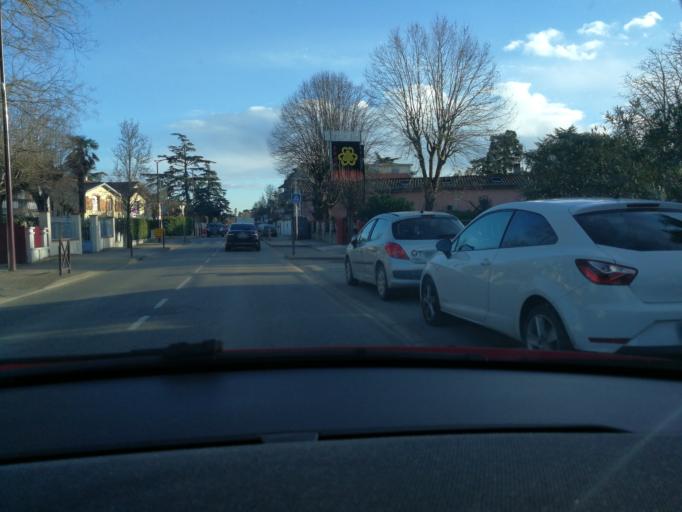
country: FR
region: Midi-Pyrenees
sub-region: Departement de la Haute-Garonne
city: Blagnac
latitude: 43.6274
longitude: 1.3982
